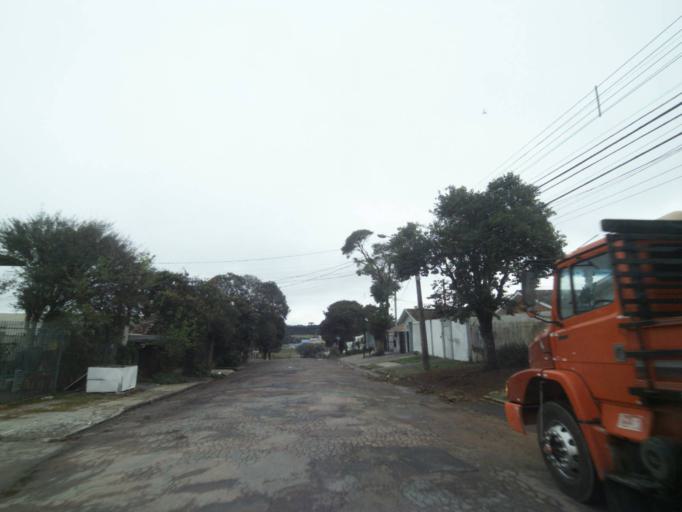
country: BR
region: Parana
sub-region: Curitiba
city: Curitiba
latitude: -25.5112
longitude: -49.3048
